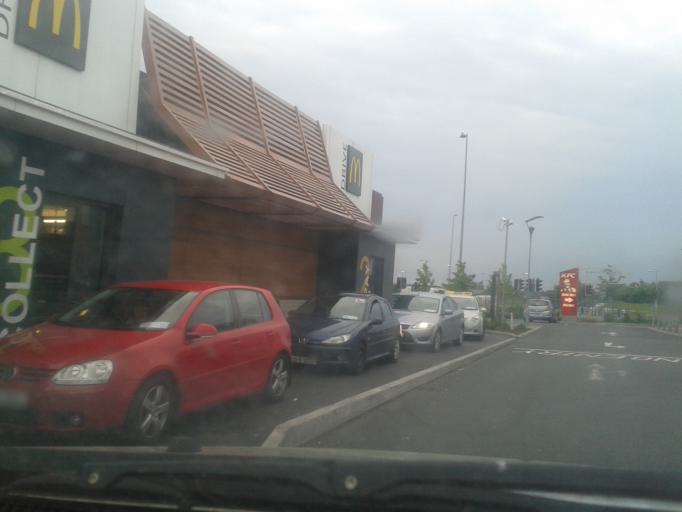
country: IE
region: Leinster
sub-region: Dublin City
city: Finglas
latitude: 53.4036
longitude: -6.3064
